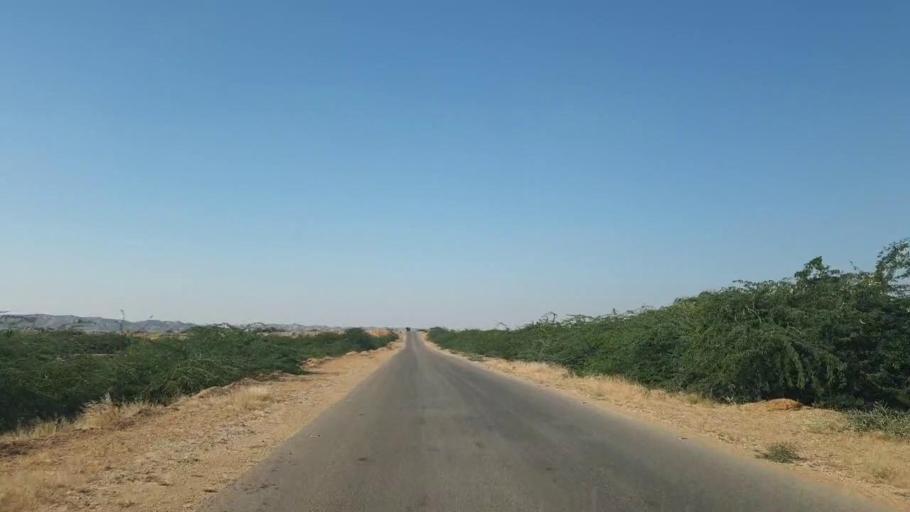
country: PK
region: Sindh
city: Malir Cantonment
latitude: 25.2776
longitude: 67.5870
